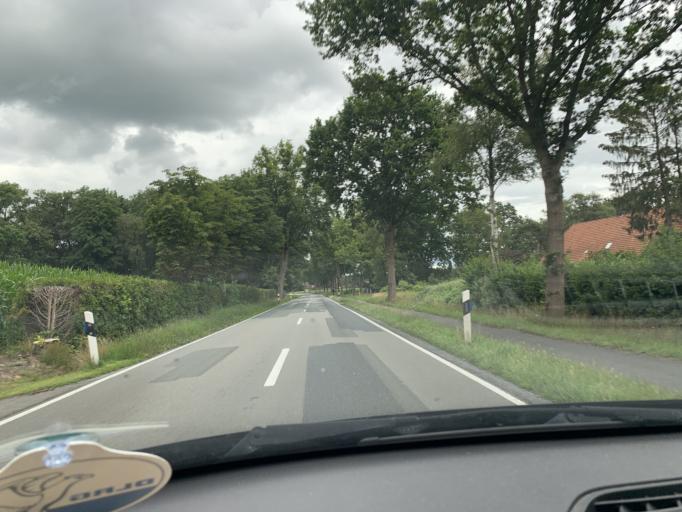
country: DE
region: Lower Saxony
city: Edewecht
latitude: 53.1401
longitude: 7.8779
